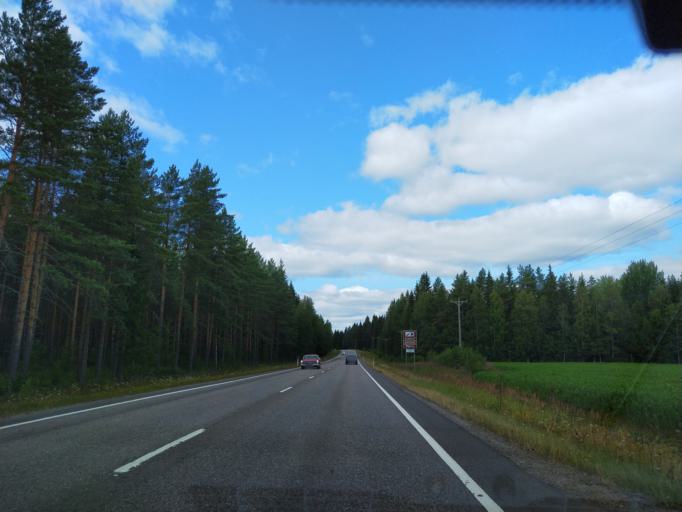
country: FI
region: Haeme
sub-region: Haemeenlinna
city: Renko
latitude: 60.7568
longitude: 24.2982
